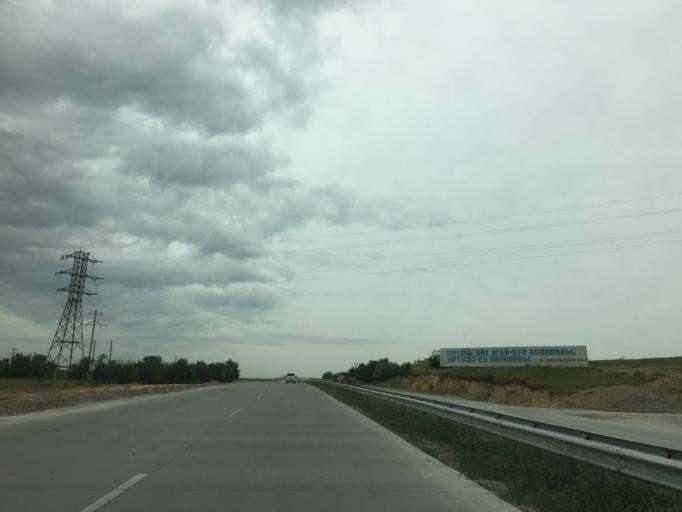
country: KZ
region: Ongtustik Qazaqstan
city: Sastobe
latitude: 42.5332
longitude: 70.0220
